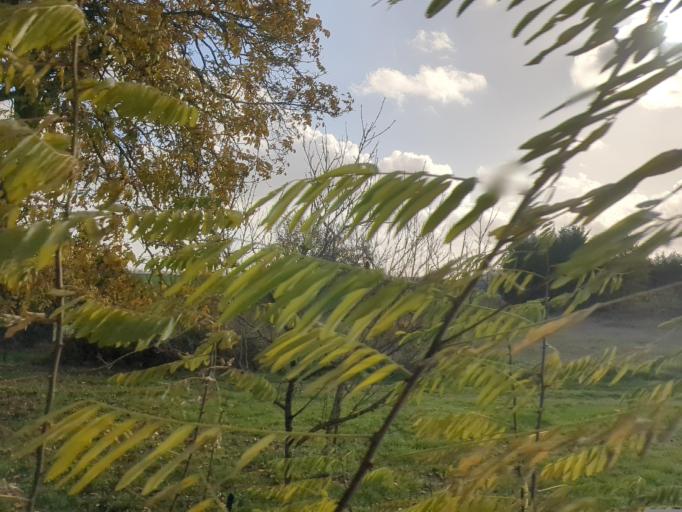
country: FR
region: Centre
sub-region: Departement d'Indre-et-Loire
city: Chanceaux-sur-Choisille
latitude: 47.4607
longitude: 0.7127
